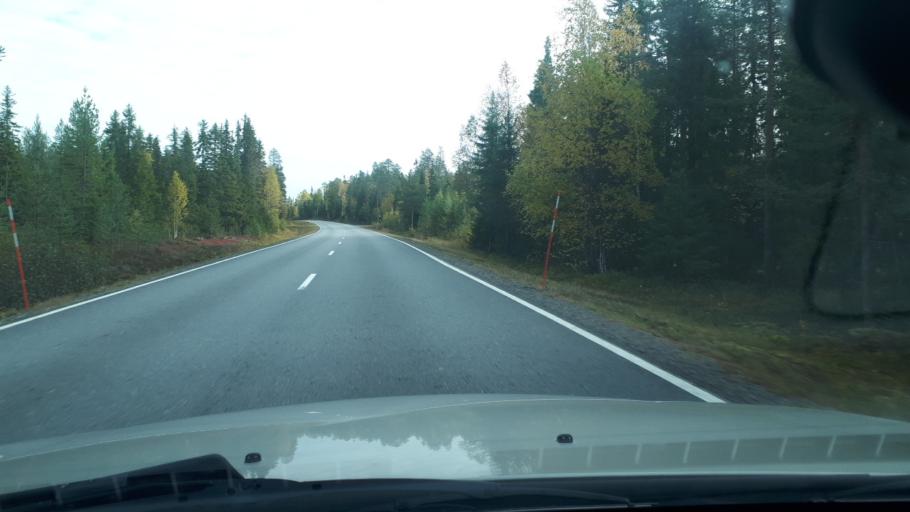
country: FI
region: Northern Ostrobothnia
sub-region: Oulu
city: Yli-Ii
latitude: 65.9277
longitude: 25.8501
